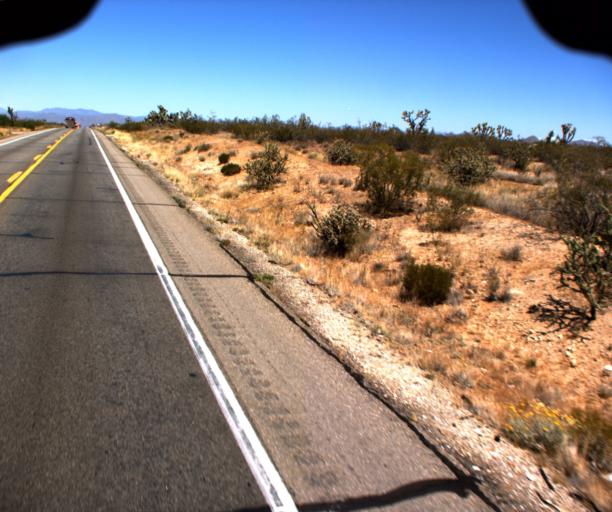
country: US
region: Arizona
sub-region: Yavapai County
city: Congress
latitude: 34.2452
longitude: -113.0788
